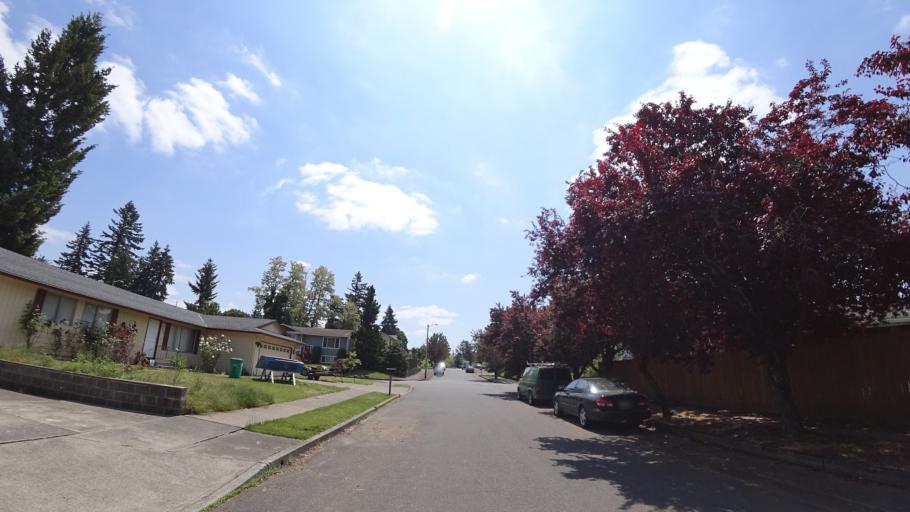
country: US
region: Oregon
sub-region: Multnomah County
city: Fairview
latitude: 45.5400
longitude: -122.4980
